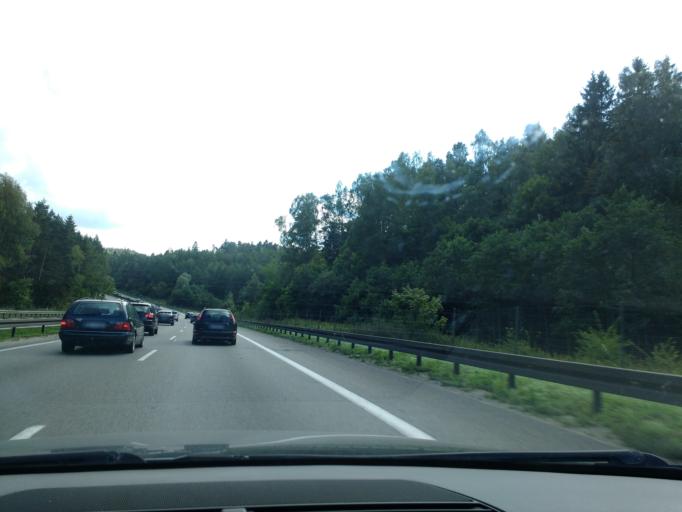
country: PL
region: Pomeranian Voivodeship
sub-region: Gdynia
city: Wielki Kack
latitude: 54.4930
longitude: 18.4624
